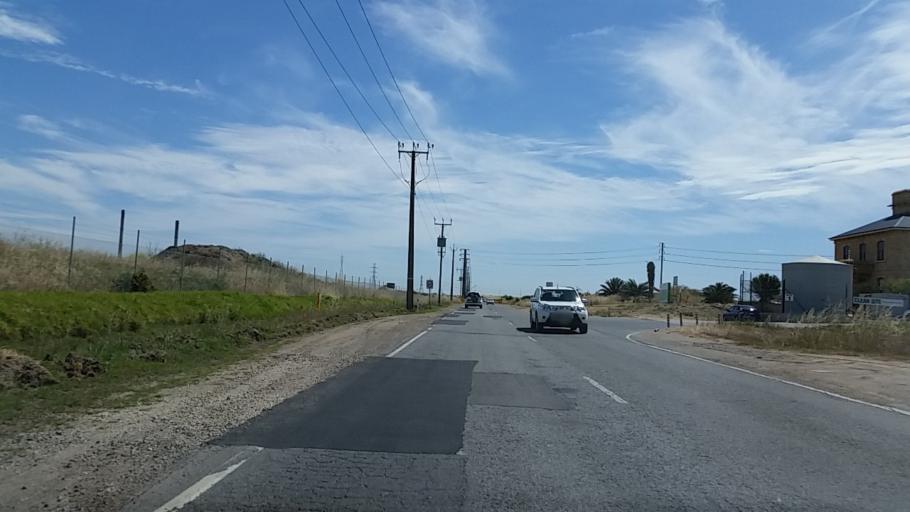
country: AU
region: South Australia
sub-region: Port Adelaide Enfield
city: Birkenhead
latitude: -34.8236
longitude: 138.5215
